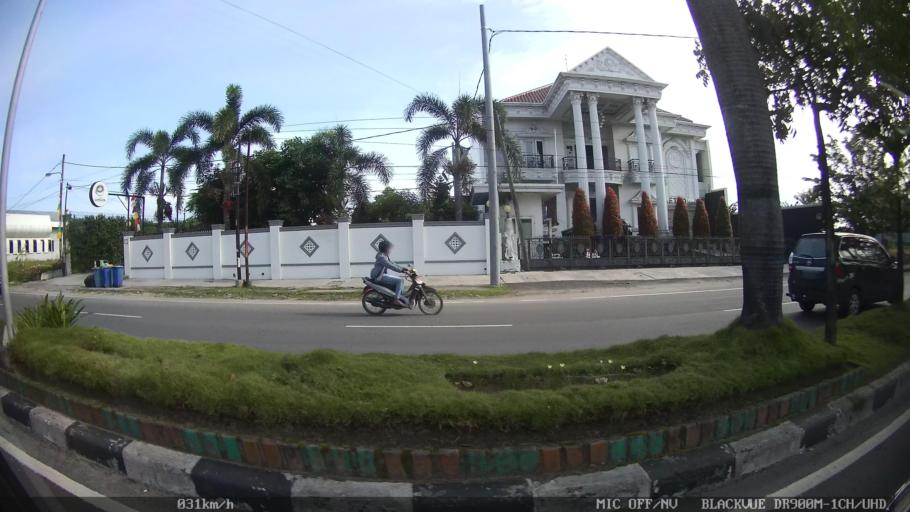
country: ID
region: North Sumatra
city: Medan
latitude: 3.6080
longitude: 98.6490
